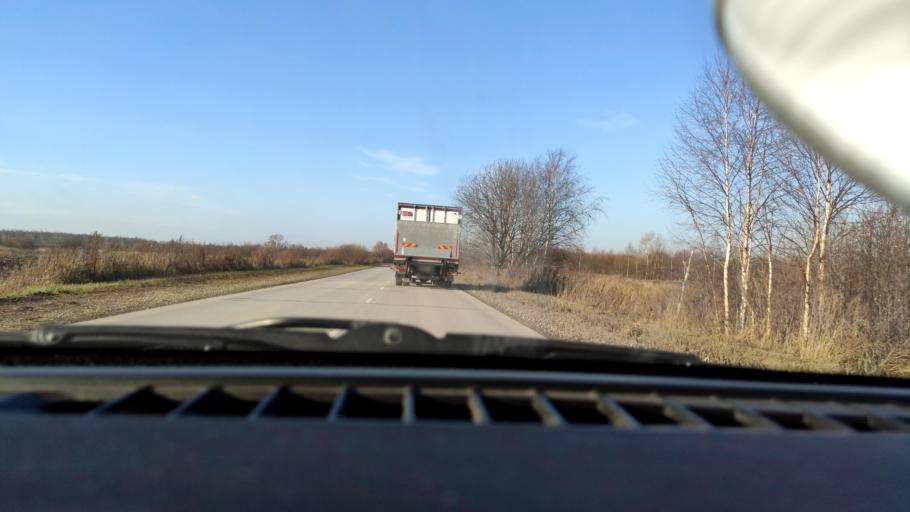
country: RU
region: Perm
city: Kondratovo
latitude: 57.9986
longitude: 56.0776
